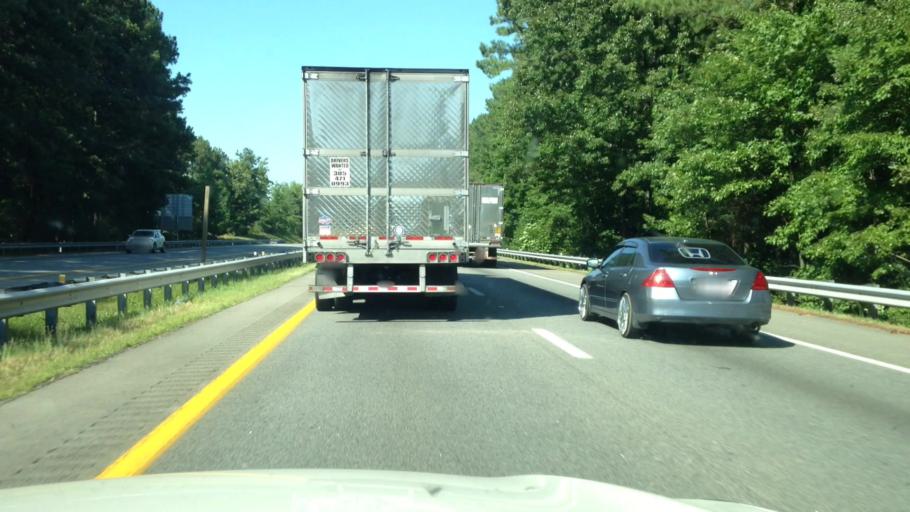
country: US
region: Virginia
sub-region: City of Emporia
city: Emporia
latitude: 36.7181
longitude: -77.5365
